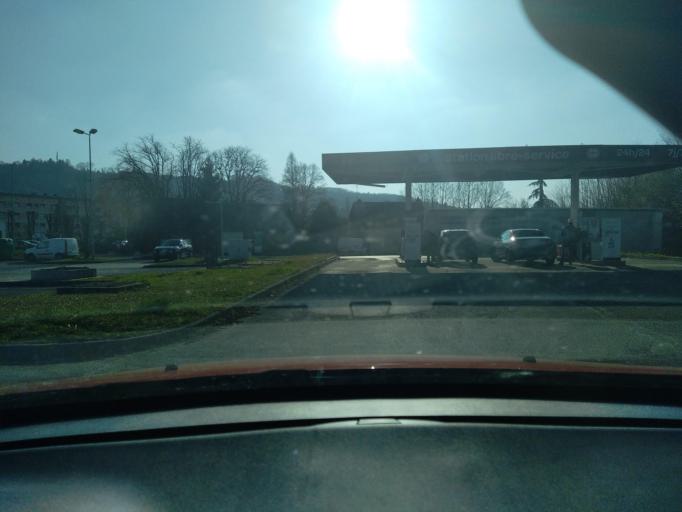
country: FR
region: Franche-Comte
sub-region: Departement du Jura
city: Perrigny
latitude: 46.6704
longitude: 5.5744
